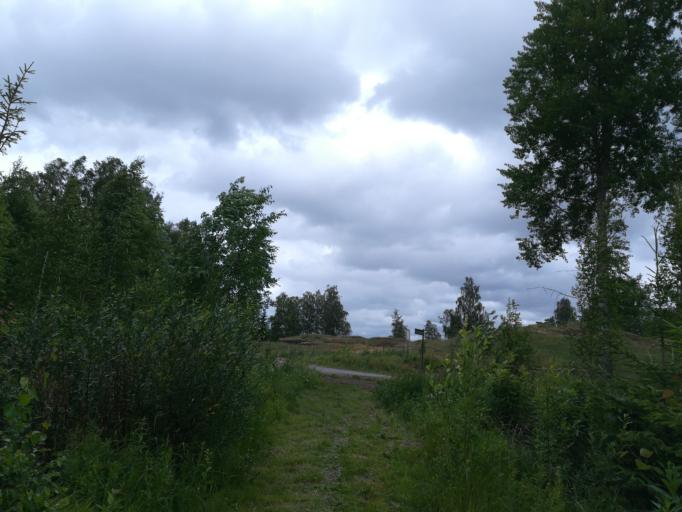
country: FI
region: South Karelia
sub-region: Lappeenranta
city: Savitaipale
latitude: 61.2613
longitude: 27.7095
